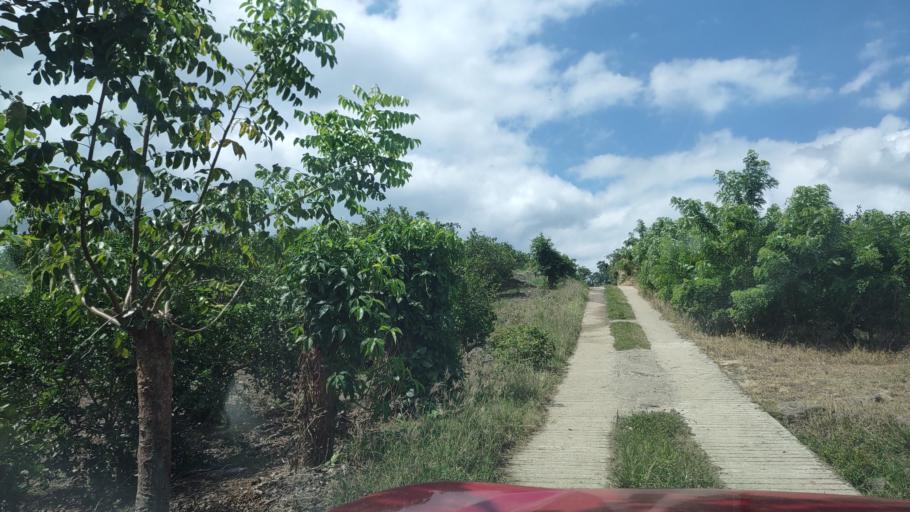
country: MX
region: Puebla
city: San Jose Acateno
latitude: 20.2195
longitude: -97.1410
